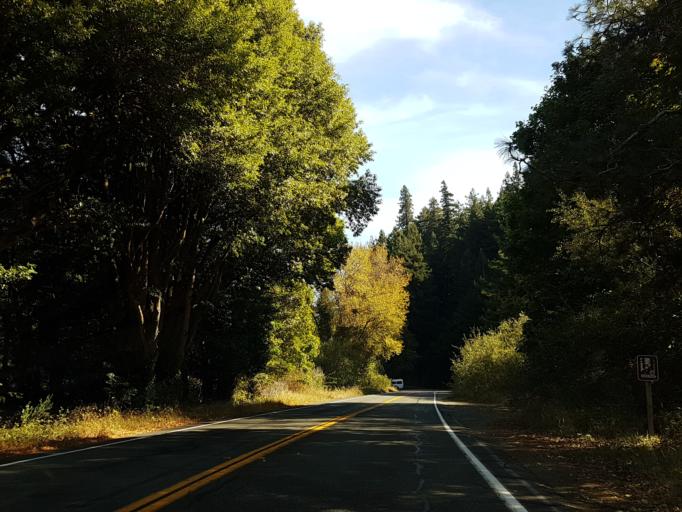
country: US
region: California
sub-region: Humboldt County
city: Rio Dell
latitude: 40.4444
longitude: -123.9873
